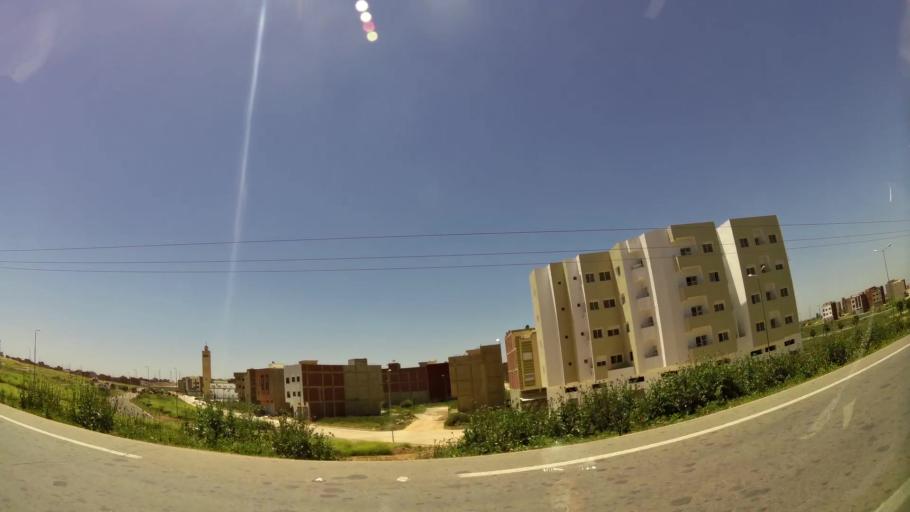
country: MA
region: Meknes-Tafilalet
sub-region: Meknes
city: Meknes
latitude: 33.8489
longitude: -5.5572
